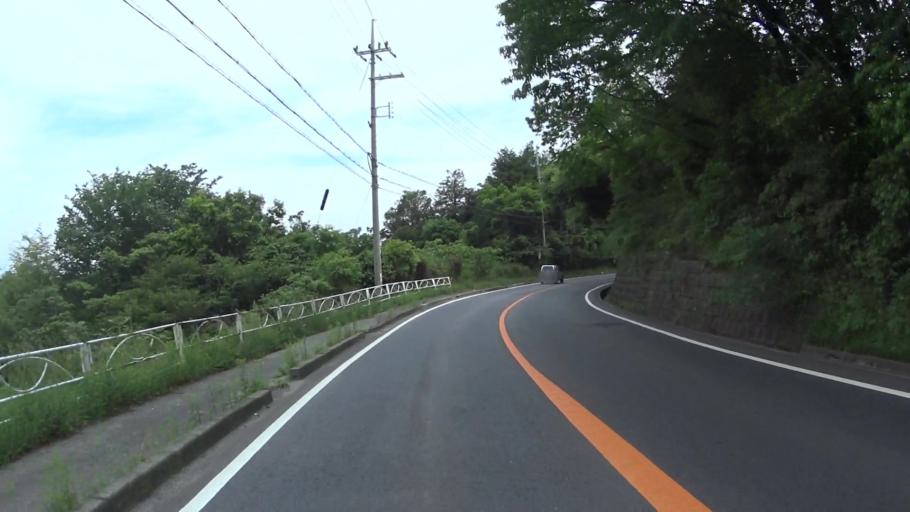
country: JP
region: Shiga Prefecture
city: Kitahama
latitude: 35.1556
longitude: 135.8764
